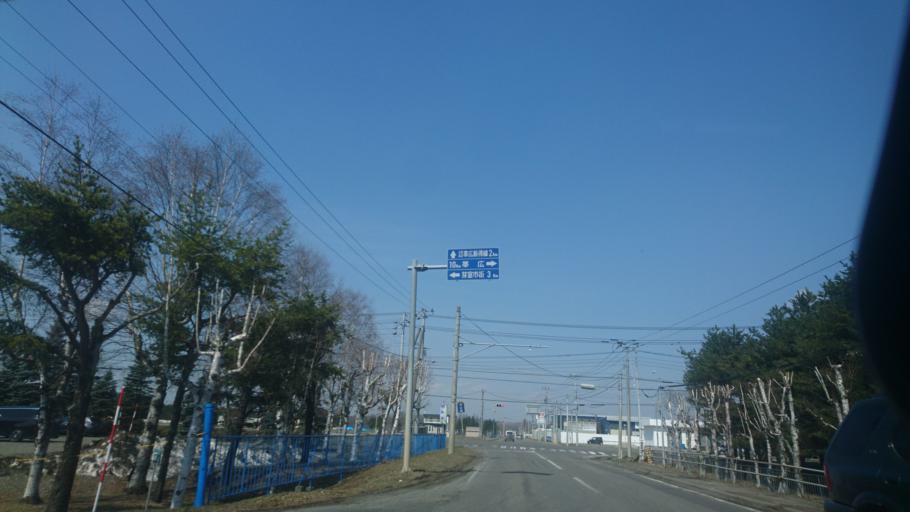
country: JP
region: Hokkaido
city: Obihiro
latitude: 42.9227
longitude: 143.0823
